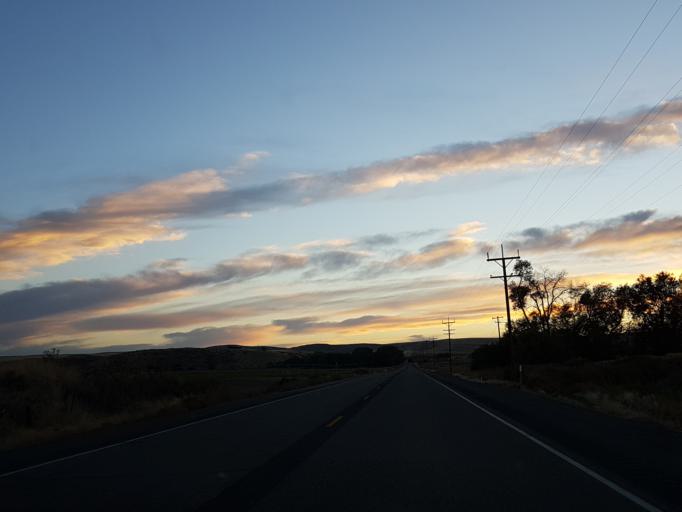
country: US
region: Oregon
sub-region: Malheur County
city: Vale
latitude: 43.9330
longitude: -117.3854
